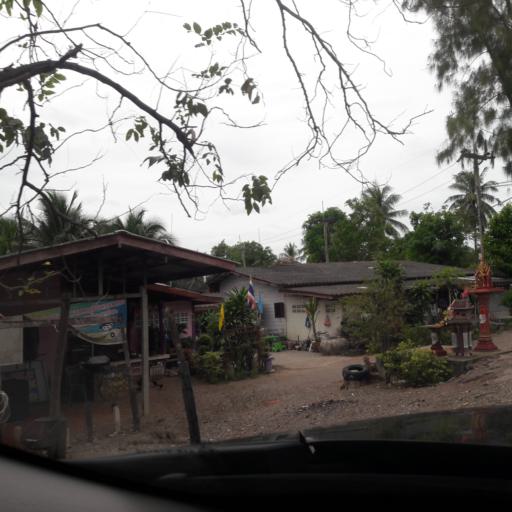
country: TH
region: Ratchaburi
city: Damnoen Saduak
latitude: 13.5757
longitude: 99.9373
